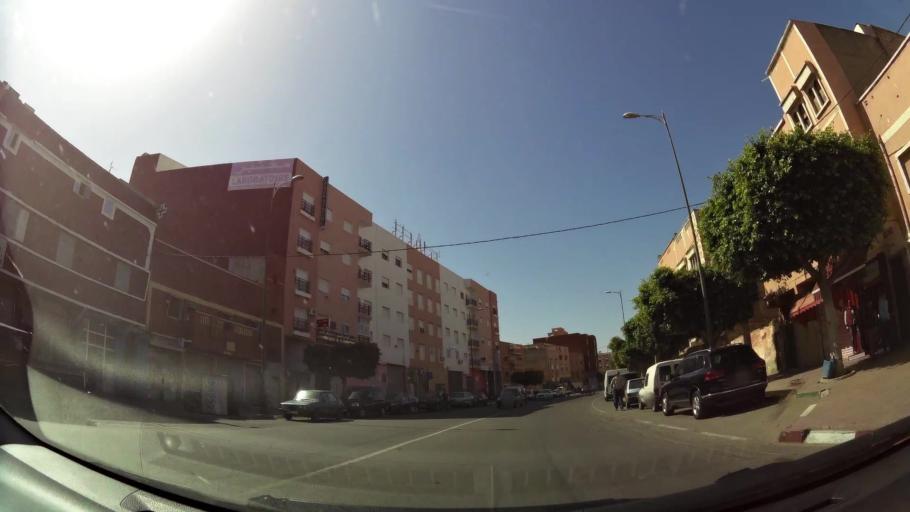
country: MA
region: Souss-Massa-Draa
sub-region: Inezgane-Ait Mellou
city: Inezgane
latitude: 30.3415
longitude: -9.5023
